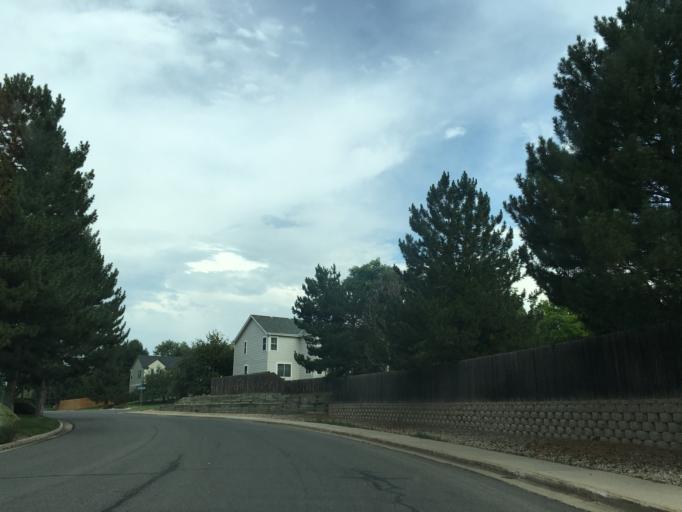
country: US
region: Colorado
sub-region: Jefferson County
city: Lakewood
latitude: 39.6743
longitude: -105.0600
